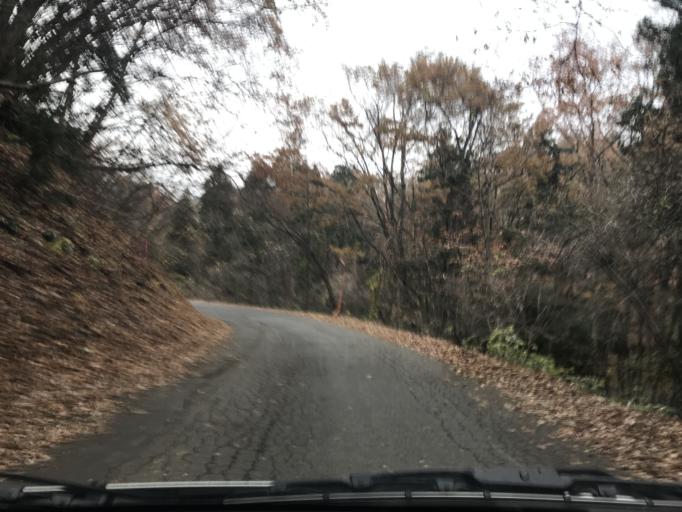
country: JP
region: Iwate
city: Ichinoseki
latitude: 38.9813
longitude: 141.0027
